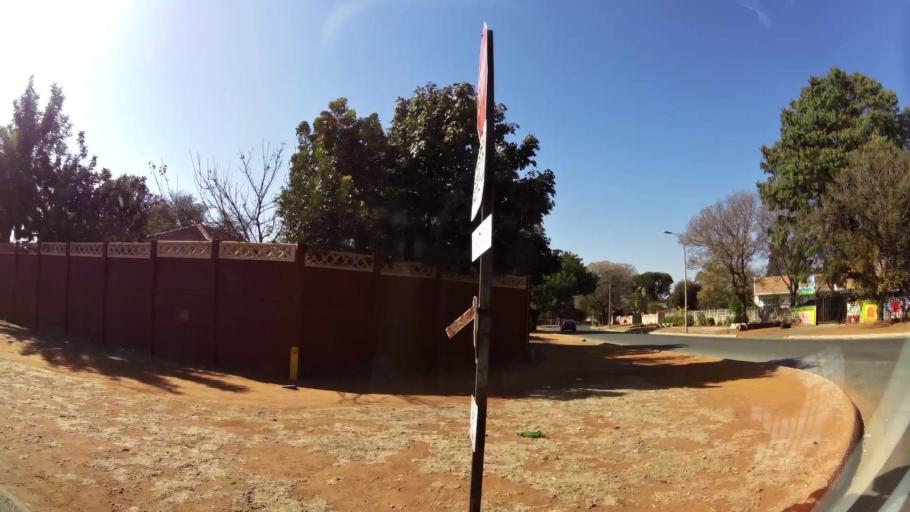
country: ZA
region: Gauteng
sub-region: Ekurhuleni Metropolitan Municipality
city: Tembisa
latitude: -26.0481
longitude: 28.2066
